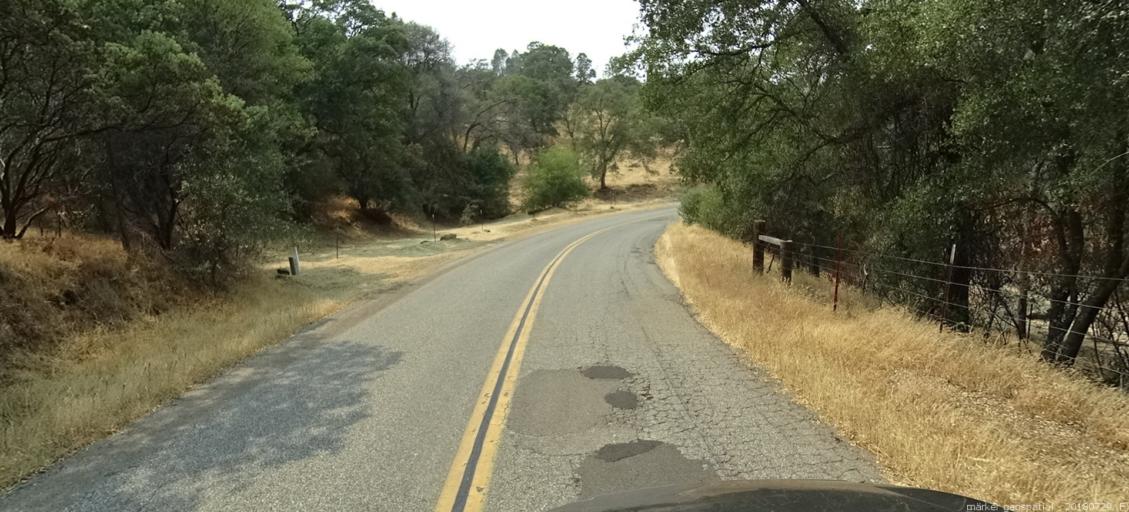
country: US
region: California
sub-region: Madera County
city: Ahwahnee
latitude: 37.3393
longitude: -119.7697
